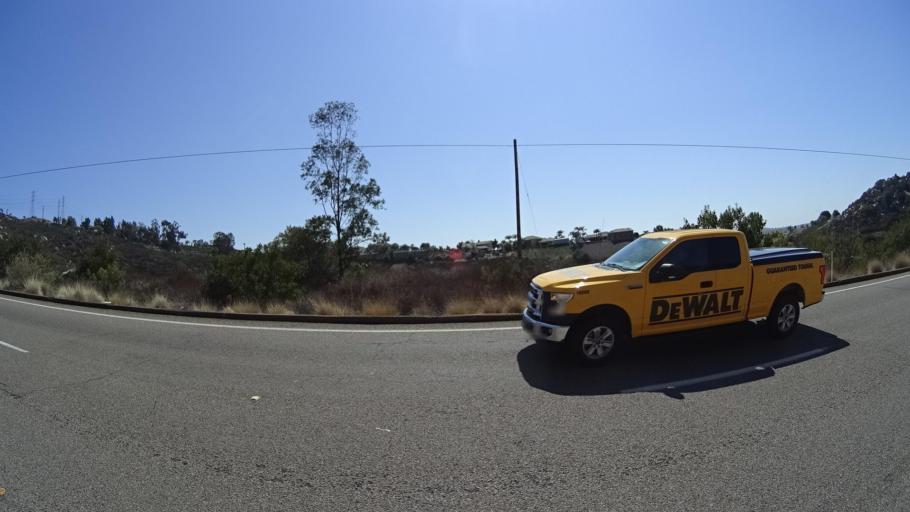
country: US
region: California
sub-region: San Diego County
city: Granite Hills
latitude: 32.8094
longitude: -116.8971
